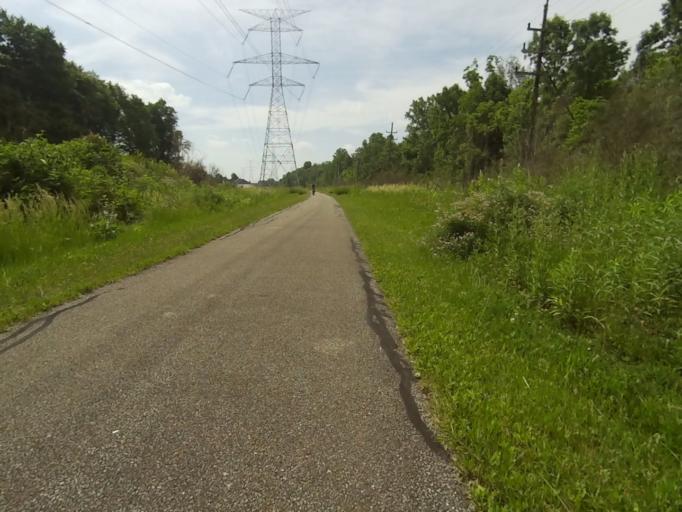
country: US
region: Ohio
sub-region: Cuyahoga County
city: Walton Hills
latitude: 41.3216
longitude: -81.5684
